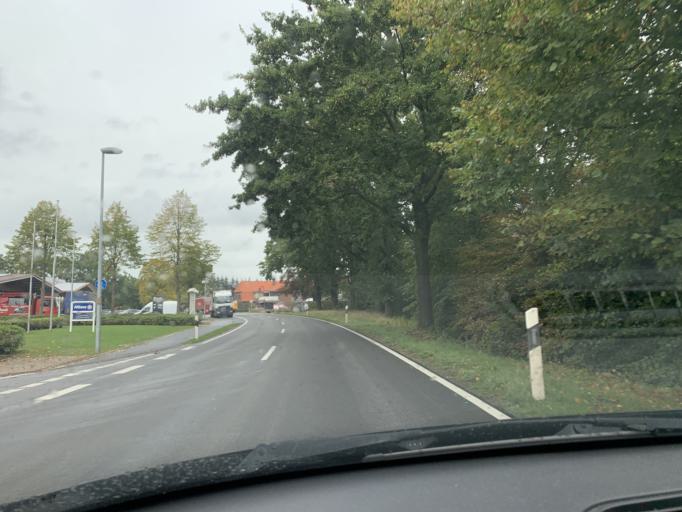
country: DE
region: Lower Saxony
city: Bad Zwischenahn
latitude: 53.1758
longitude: 8.0694
